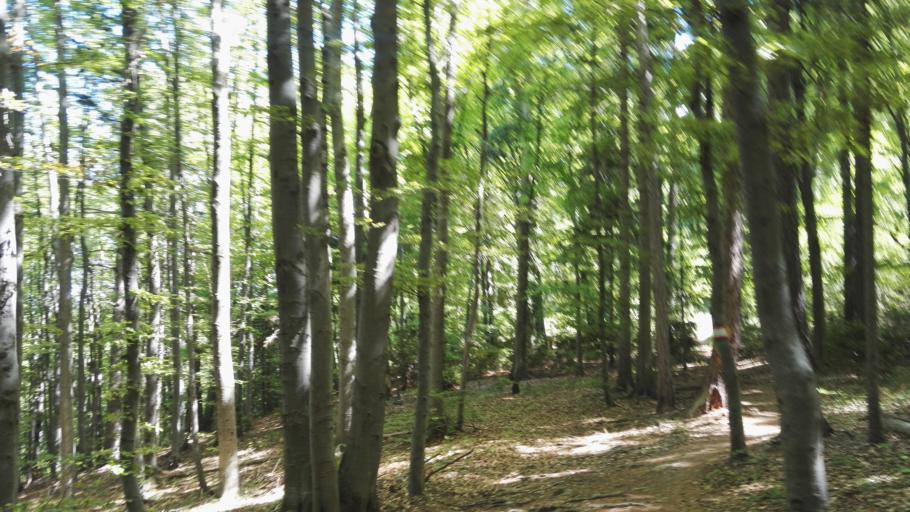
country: AT
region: Styria
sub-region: Politischer Bezirk Graz-Umgebung
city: Thal
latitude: 47.0837
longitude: 15.3797
